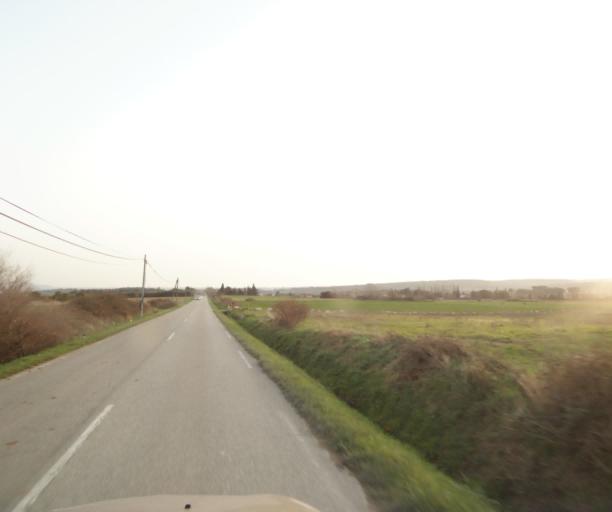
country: FR
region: Provence-Alpes-Cote d'Azur
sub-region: Departement des Bouches-du-Rhone
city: Eguilles
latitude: 43.5563
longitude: 5.3506
